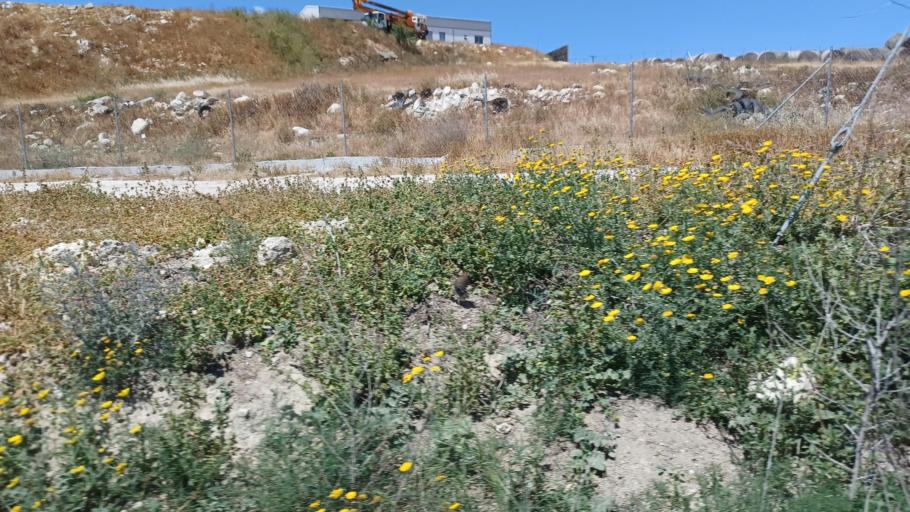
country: CY
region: Larnaka
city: Athienou
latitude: 35.0366
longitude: 33.5436
